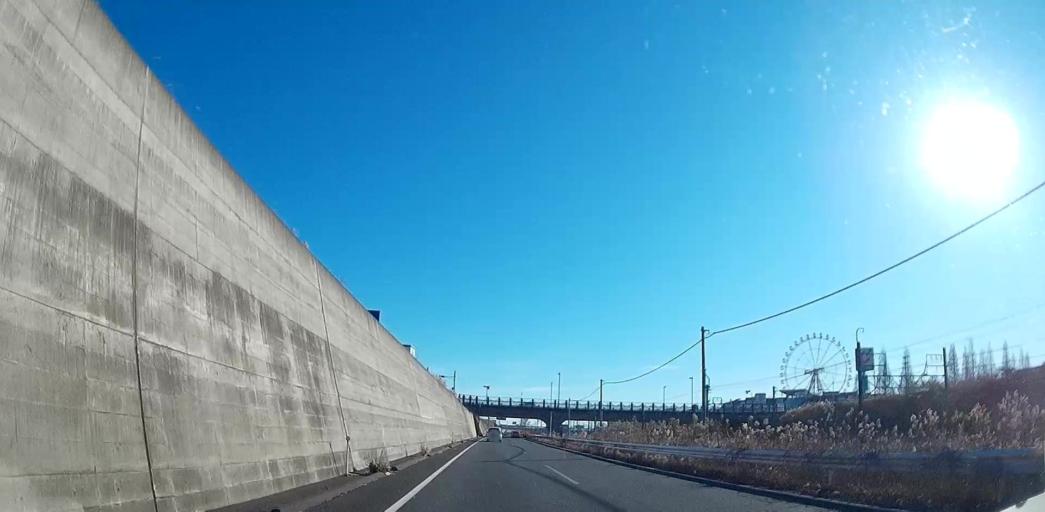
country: JP
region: Chiba
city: Shiroi
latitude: 35.8055
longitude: 140.1587
